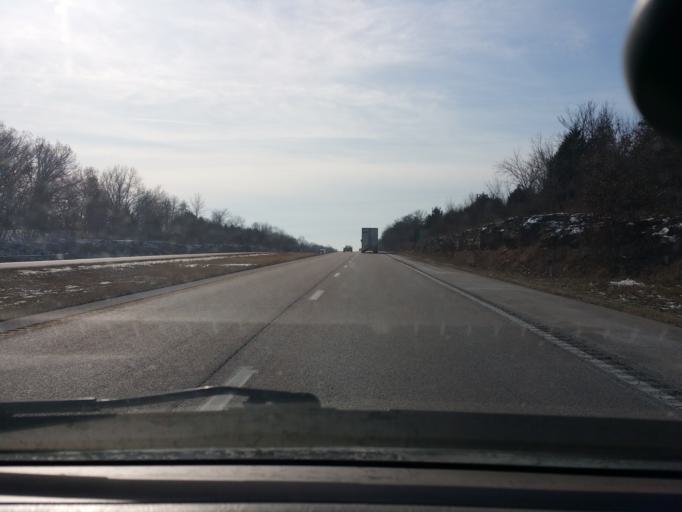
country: US
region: Missouri
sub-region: Clinton County
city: Lathrop
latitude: 39.4907
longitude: -94.3016
